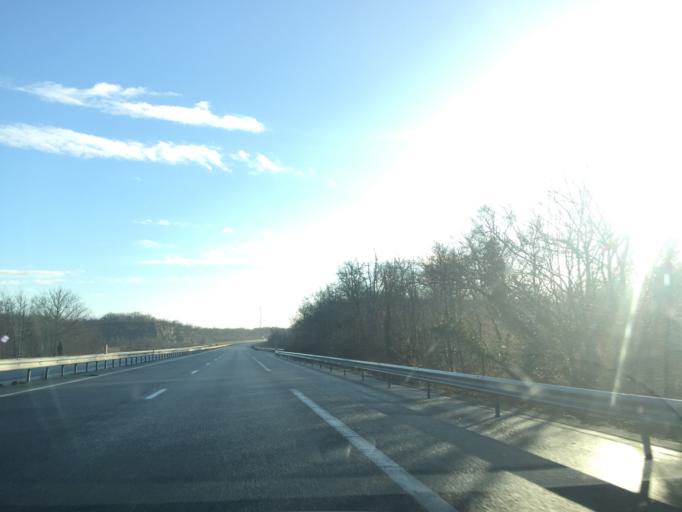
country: FR
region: Aquitaine
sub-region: Departement de la Dordogne
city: Thenon
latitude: 45.1637
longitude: 1.0437
